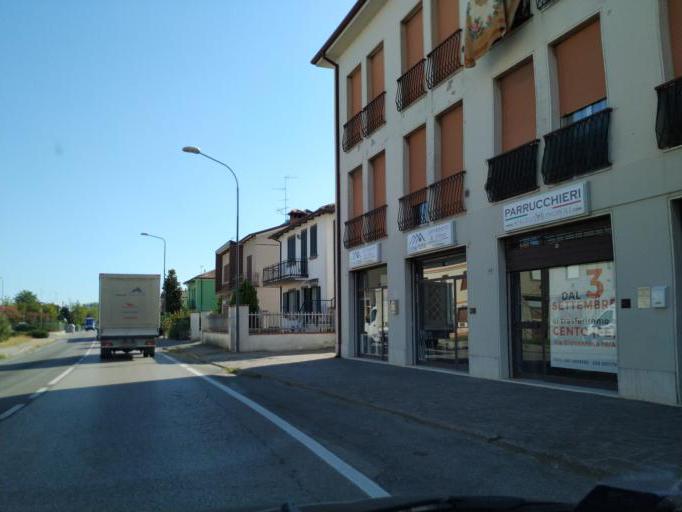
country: IT
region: Emilia-Romagna
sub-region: Provincia di Ferrara
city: Dosso
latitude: 44.7678
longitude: 11.3353
